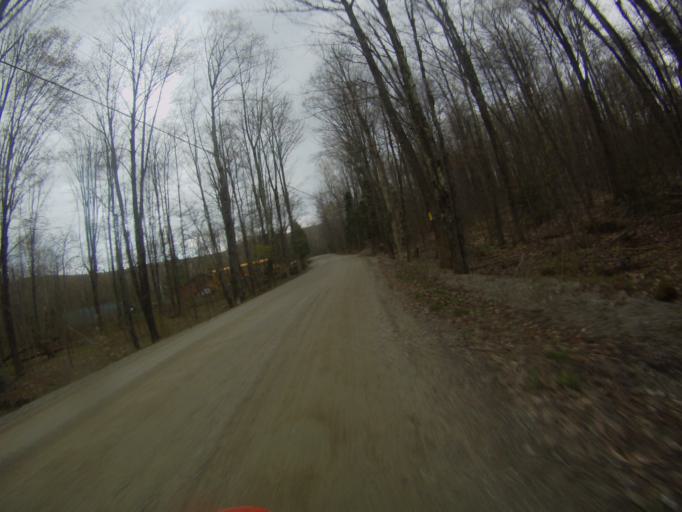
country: US
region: Vermont
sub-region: Addison County
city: Bristol
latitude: 44.0645
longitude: -73.0467
